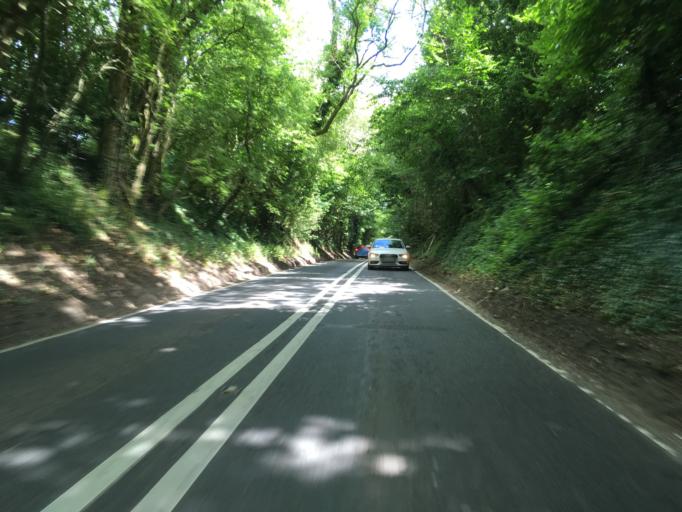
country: GB
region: England
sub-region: Hampshire
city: Highclere
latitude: 51.3140
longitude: -1.3861
